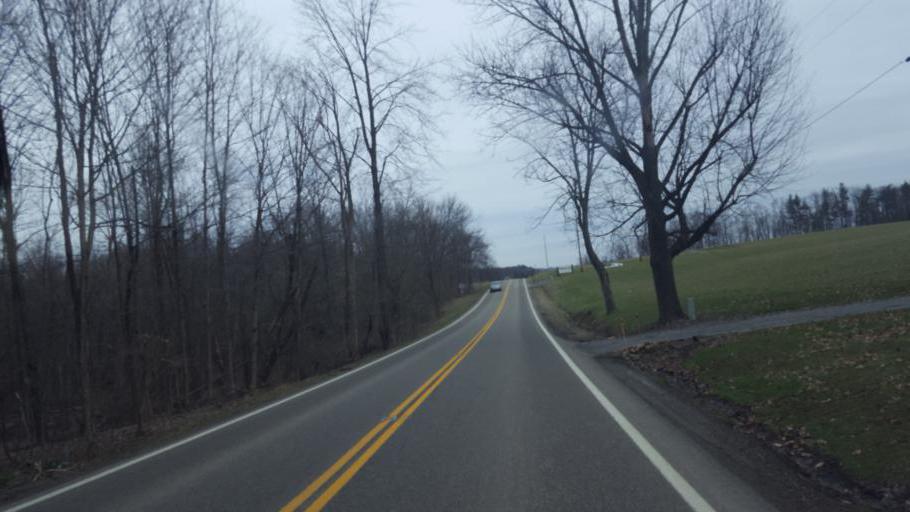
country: US
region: Ohio
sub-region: Tuscarawas County
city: Sugarcreek
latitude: 40.5581
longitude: -81.7208
